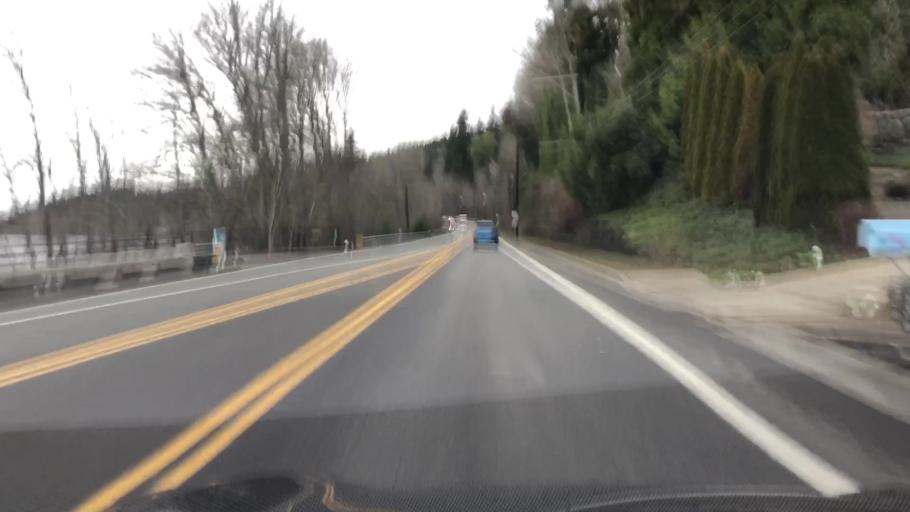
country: US
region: Washington
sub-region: King County
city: Sammamish
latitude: 47.6290
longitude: -122.0702
